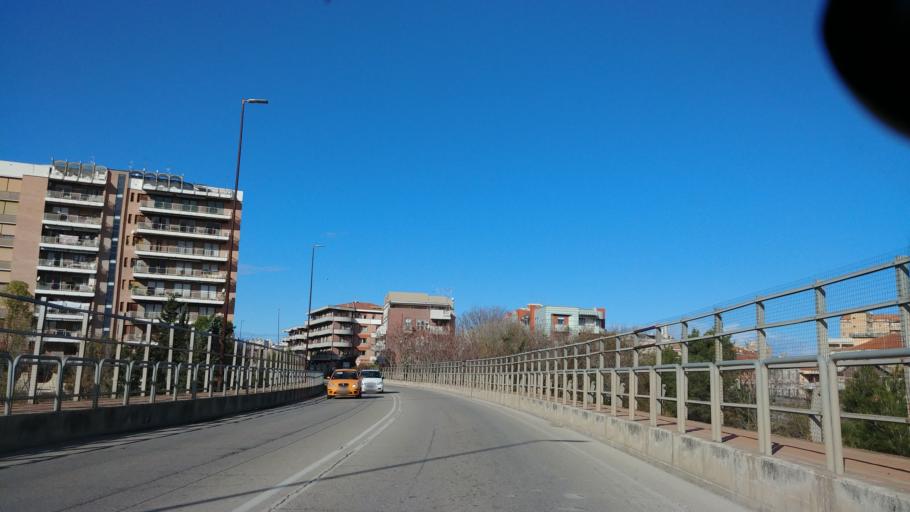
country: IT
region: Molise
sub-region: Provincia di Campobasso
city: Termoli
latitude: 41.9962
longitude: 14.9964
